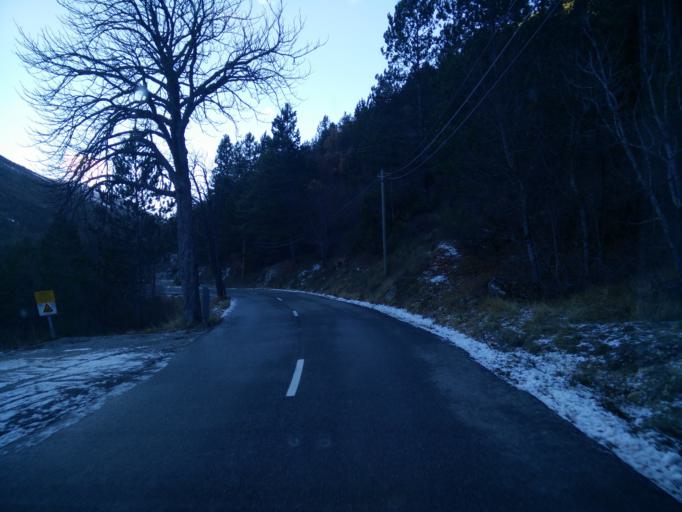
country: FR
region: Provence-Alpes-Cote d'Azur
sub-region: Departement des Alpes-de-Haute-Provence
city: Castellane
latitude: 43.8354
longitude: 6.4846
